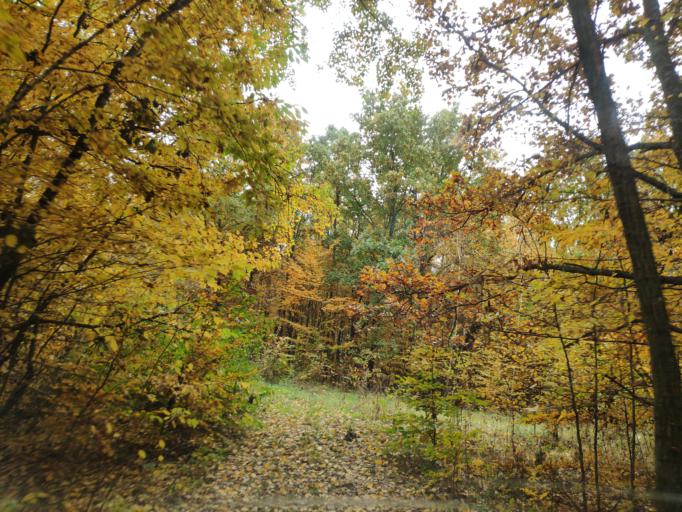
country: SK
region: Kosicky
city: Moldava nad Bodvou
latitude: 48.7247
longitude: 21.0972
